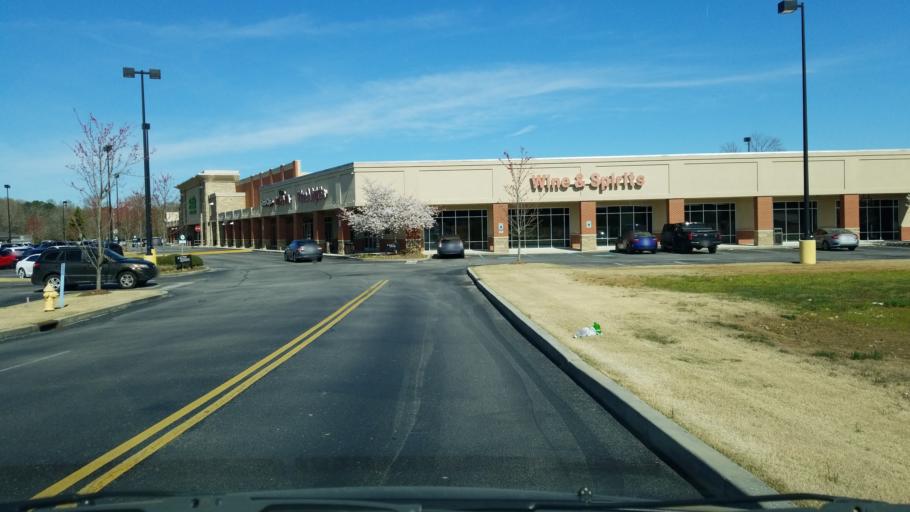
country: US
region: Tennessee
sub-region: Hamilton County
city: Collegedale
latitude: 35.0897
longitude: -85.0635
